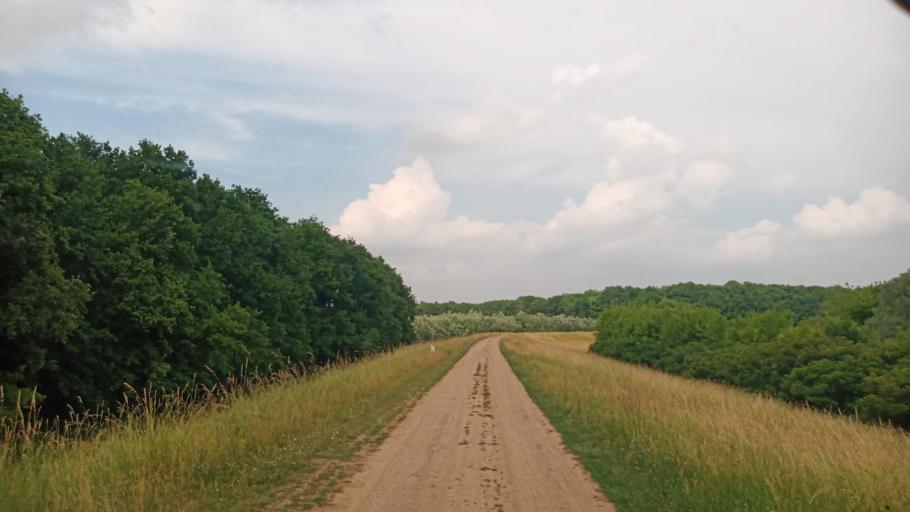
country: HU
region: Bekes
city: Doboz
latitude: 46.7061
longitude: 21.2797
